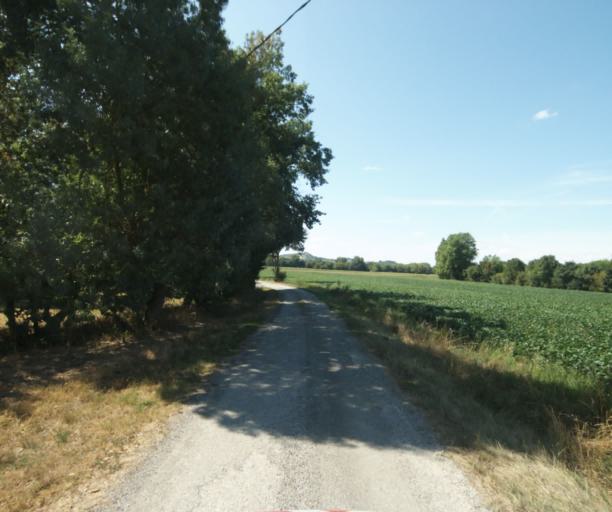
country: FR
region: Midi-Pyrenees
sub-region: Departement de la Haute-Garonne
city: Revel
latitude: 43.4905
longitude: 1.9686
